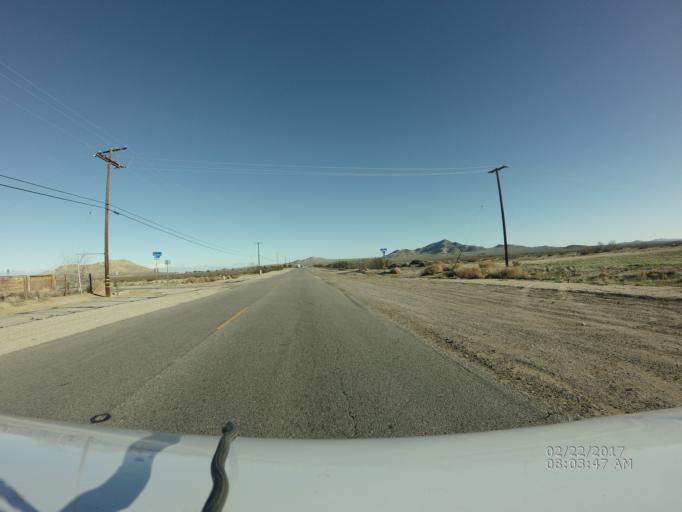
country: US
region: California
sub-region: Los Angeles County
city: Lake Los Angeles
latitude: 34.6310
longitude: -117.8272
